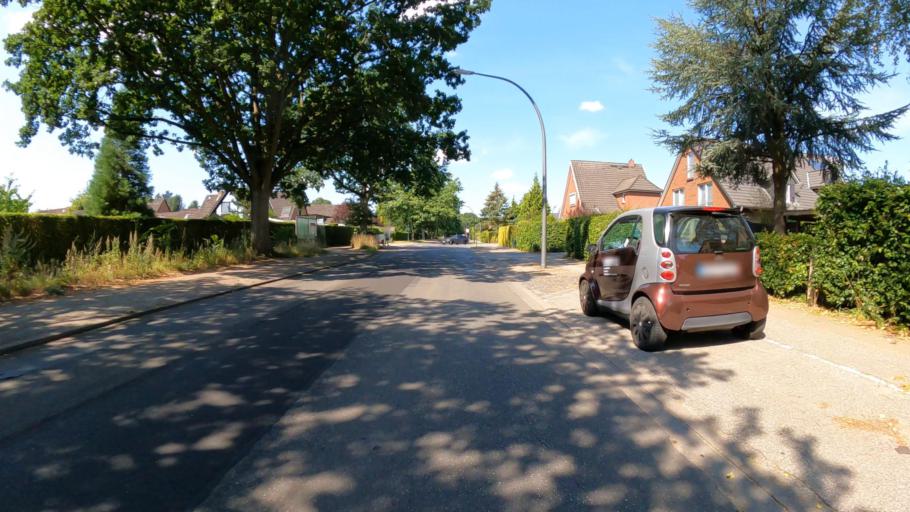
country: DE
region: Hamburg
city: Eidelstedt
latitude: 53.6145
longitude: 9.8818
